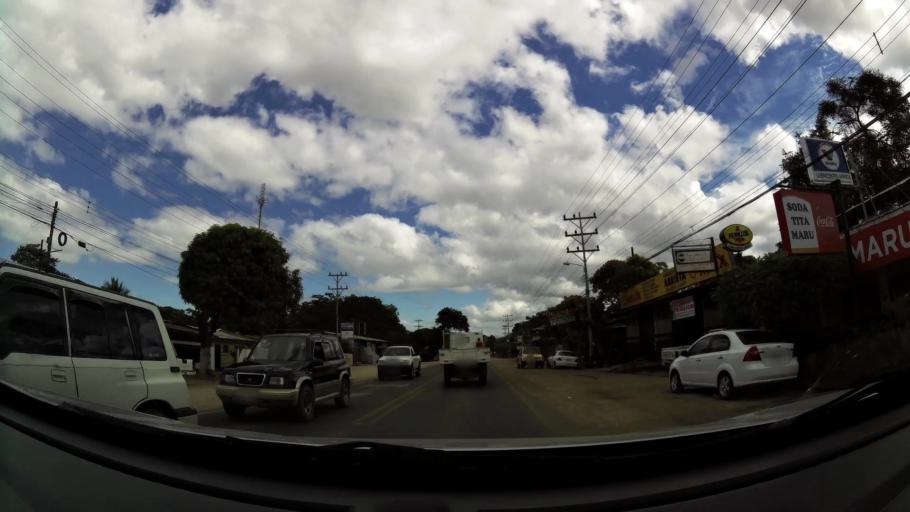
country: CR
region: Guanacaste
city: Santa Cruz
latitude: 10.2680
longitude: -85.5843
